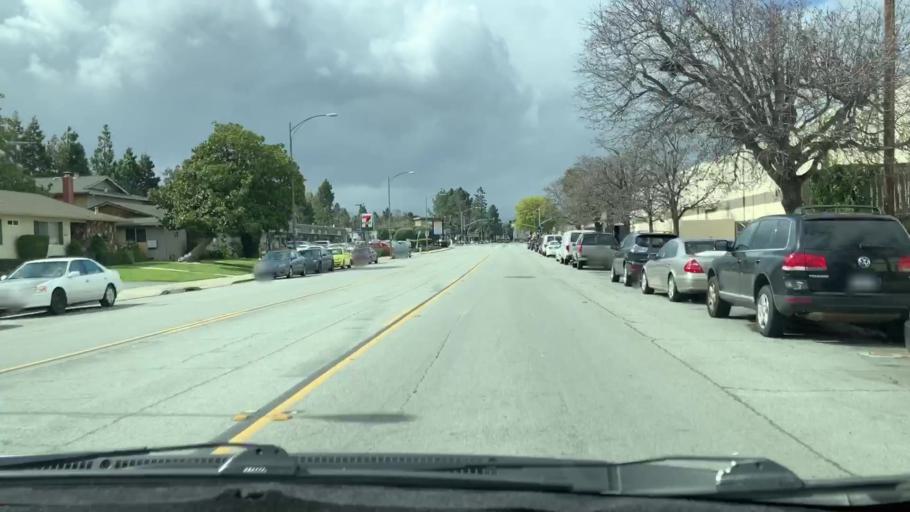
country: US
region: California
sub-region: Santa Clara County
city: Santa Clara
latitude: 37.3202
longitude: -121.9699
